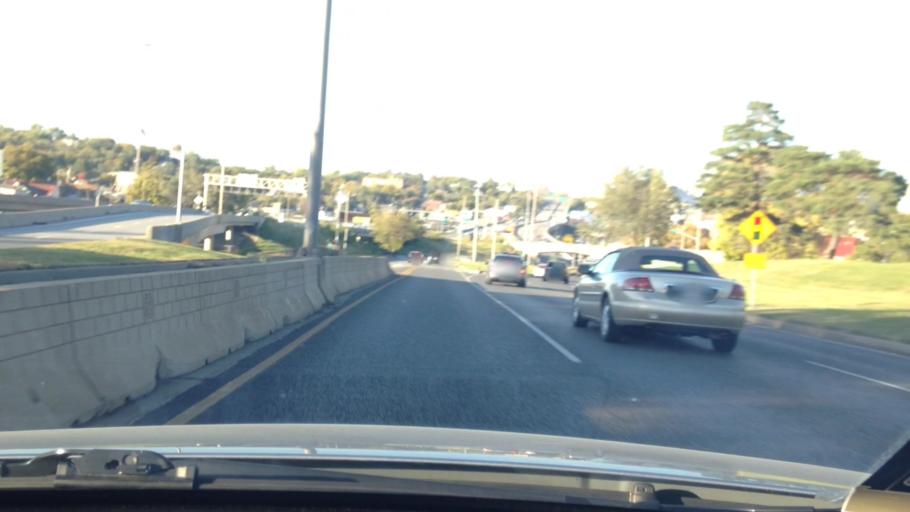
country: US
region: Missouri
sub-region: Jackson County
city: Kansas City
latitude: 39.0773
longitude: -94.5940
